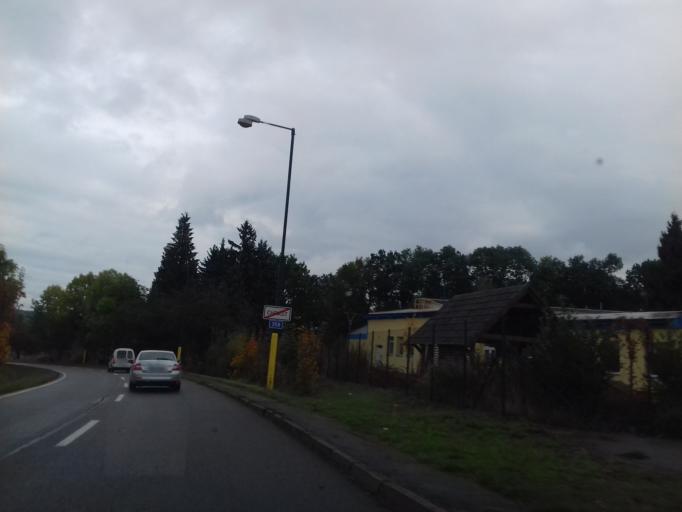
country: CZ
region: Pardubicky
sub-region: Okres Chrudim
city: Chrast
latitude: 49.8983
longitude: 15.9462
